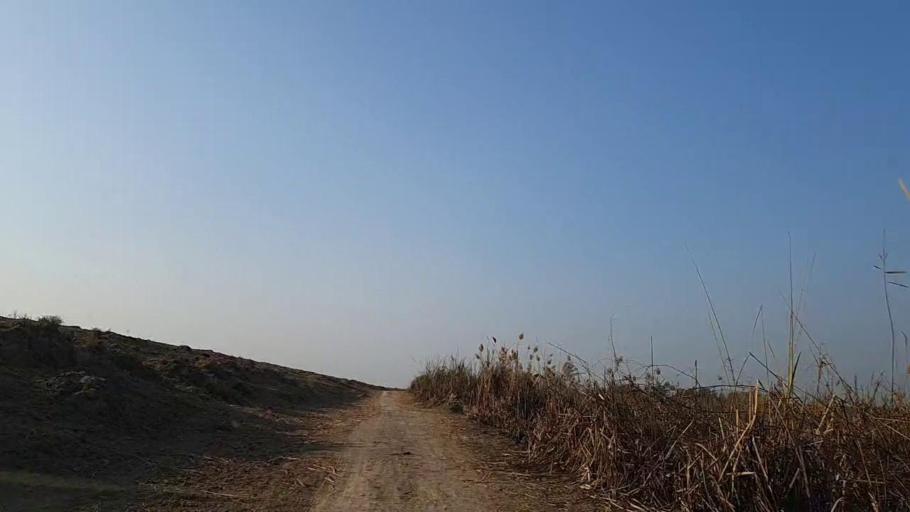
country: PK
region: Sindh
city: Sakrand
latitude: 26.0995
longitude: 68.3683
